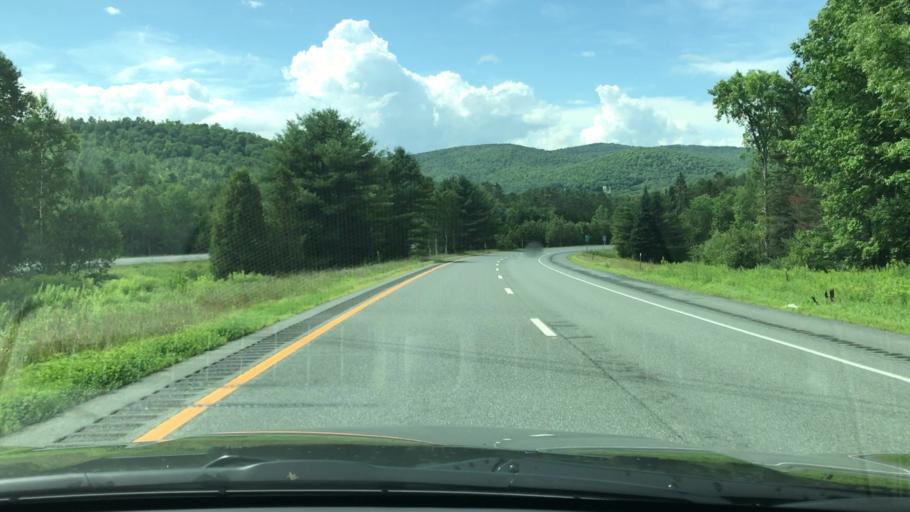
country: US
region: New Hampshire
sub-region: Grafton County
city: Littleton
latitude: 44.3350
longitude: -71.8858
